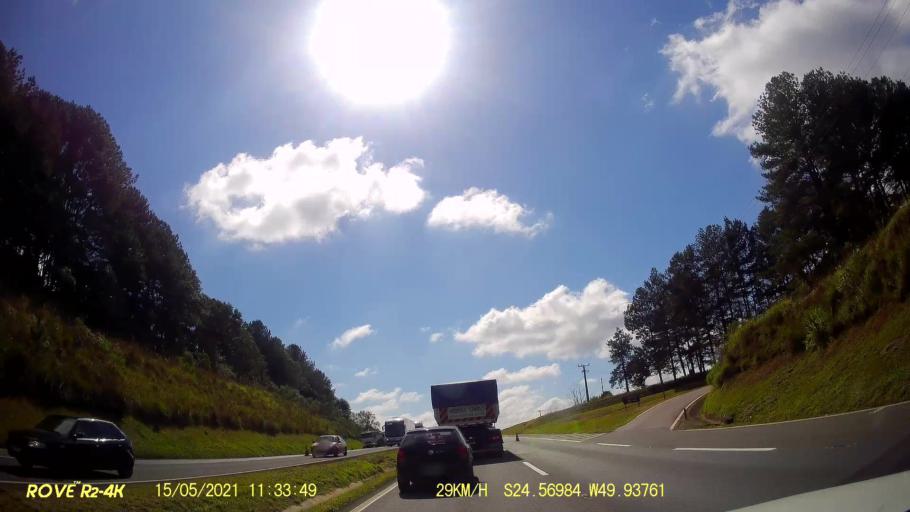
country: BR
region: Parana
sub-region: Pirai Do Sul
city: Pirai do Sul
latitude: -24.5698
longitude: -49.9376
